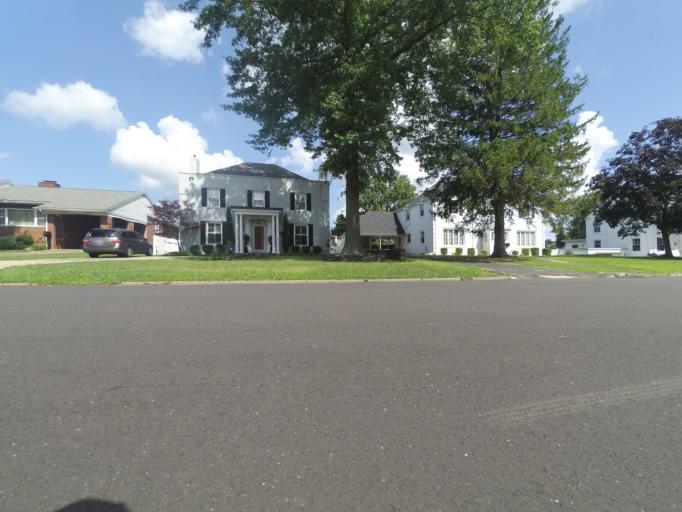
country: US
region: West Virginia
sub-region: Cabell County
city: Huntington
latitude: 38.4083
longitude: -82.4104
